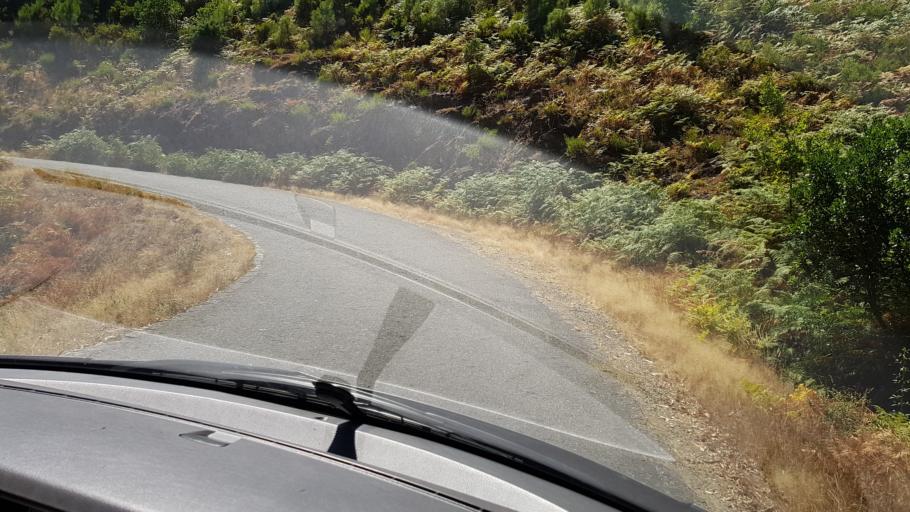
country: PT
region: Vila Real
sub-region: Mondim de Basto
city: Mondim de Basto
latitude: 41.3722
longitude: -7.8874
